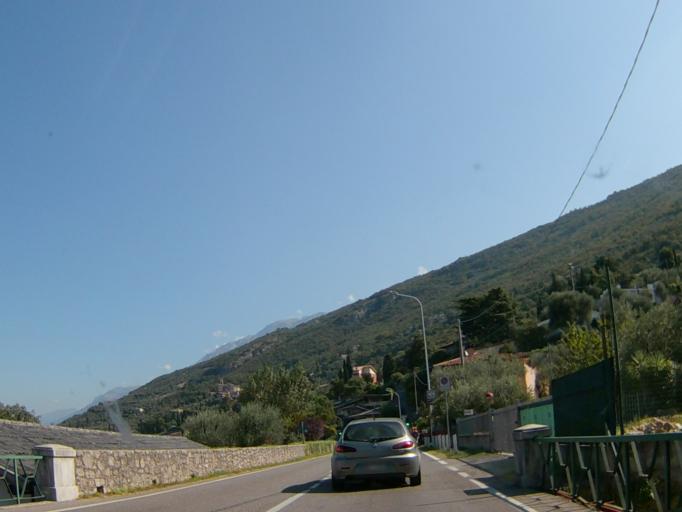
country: IT
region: Veneto
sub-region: Provincia di Verona
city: San Zeno di Montagna
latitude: 45.6481
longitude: 10.7172
